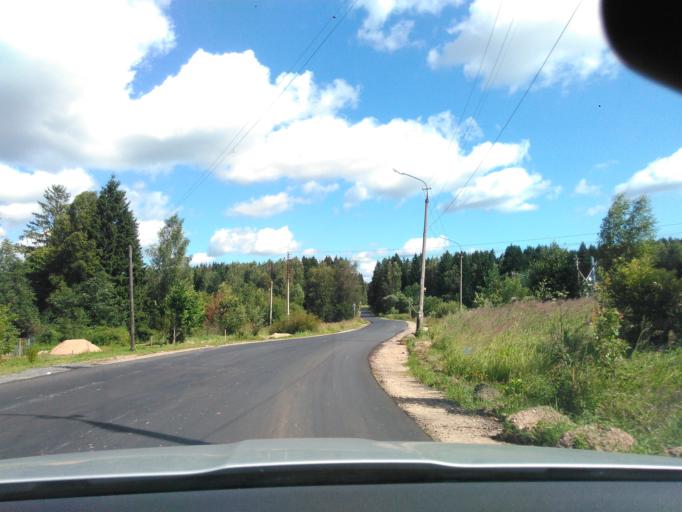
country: RU
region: Moskovskaya
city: Klin
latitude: 56.2447
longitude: 36.8317
